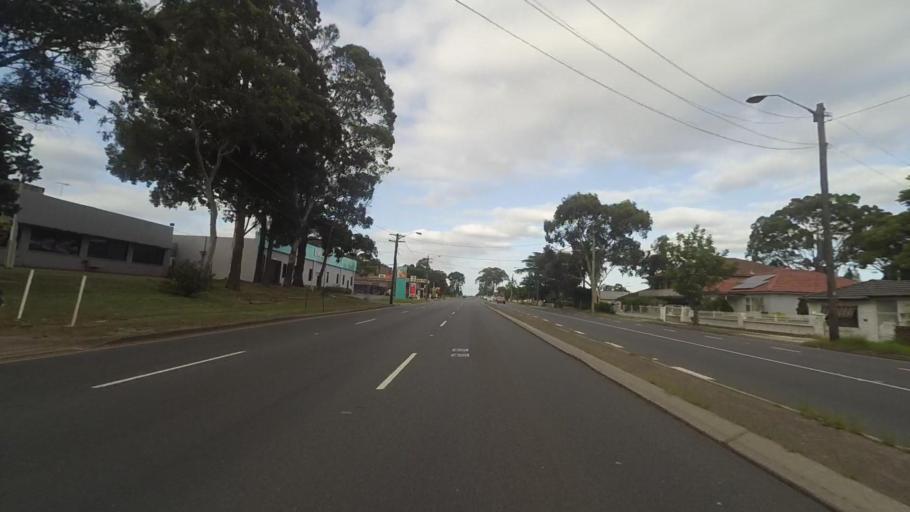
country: AU
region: New South Wales
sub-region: Bankstown
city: Revesby
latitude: -33.9378
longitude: 151.0201
